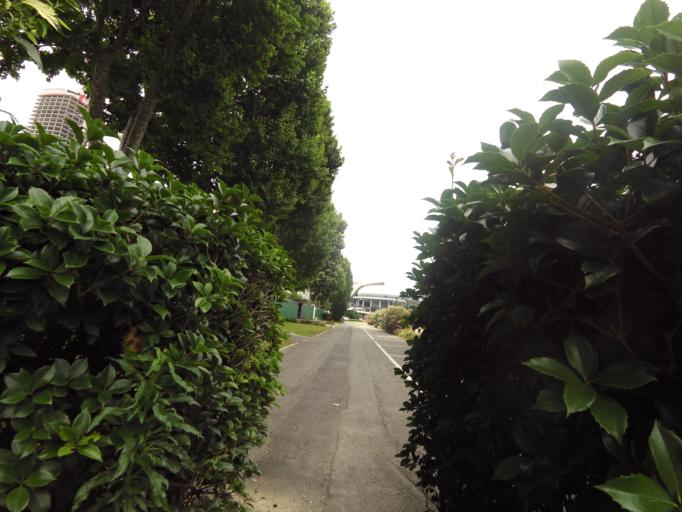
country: IT
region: Lombardy
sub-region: Citta metropolitana di Milano
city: Milano
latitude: 45.4802
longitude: 9.1584
